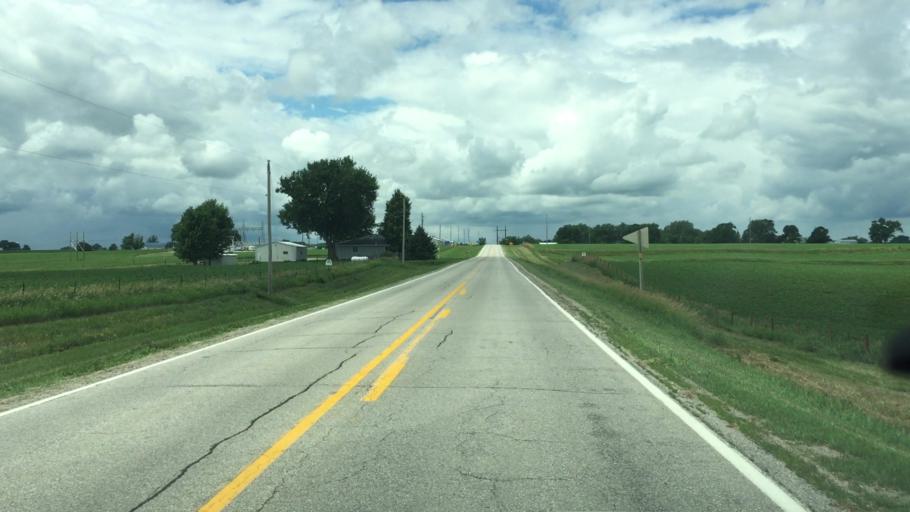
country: US
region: Iowa
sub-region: Jasper County
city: Monroe
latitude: 41.5736
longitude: -93.0899
